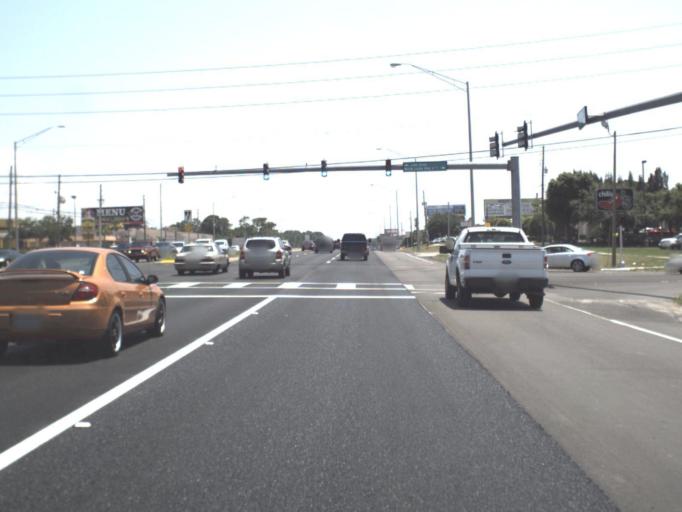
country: US
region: Florida
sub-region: Pinellas County
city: Tarpon Springs
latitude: 28.1418
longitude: -82.7404
